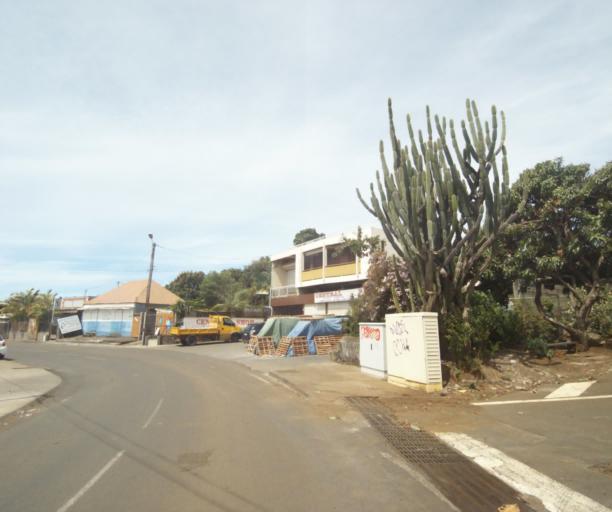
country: RE
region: Reunion
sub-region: Reunion
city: Saint-Paul
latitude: -21.0465
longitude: 55.2857
